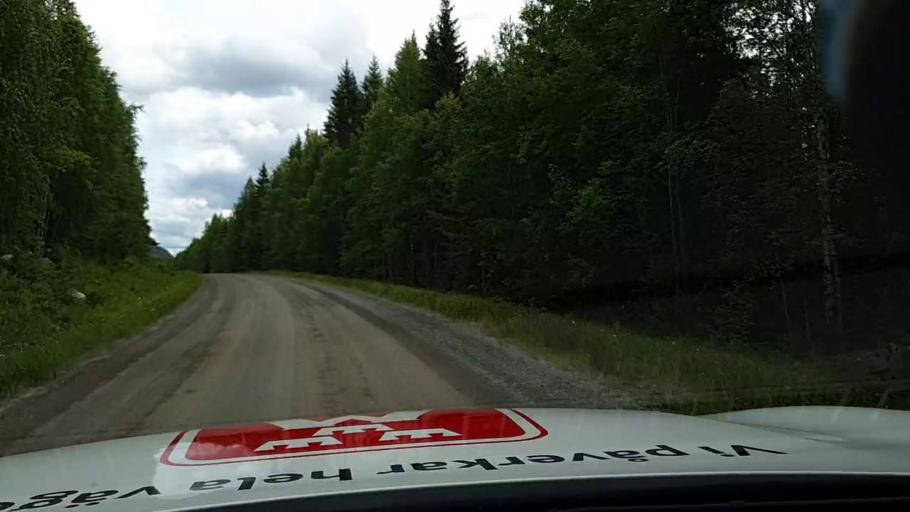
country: SE
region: Jaemtland
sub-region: Braecke Kommun
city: Braecke
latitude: 63.2115
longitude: 15.3744
